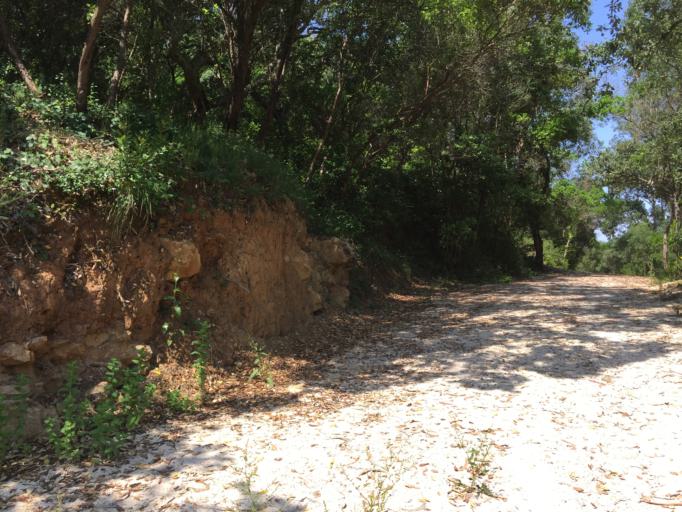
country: PT
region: Lisbon
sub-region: Mafra
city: Milharado
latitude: 38.9062
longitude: -9.1847
